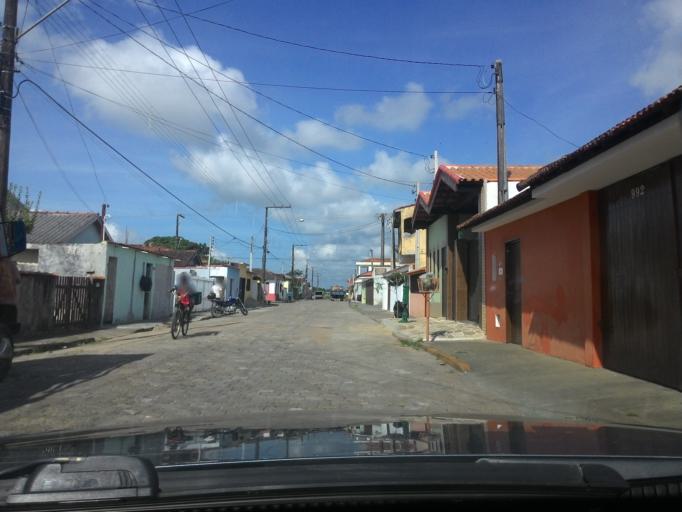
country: BR
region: Sao Paulo
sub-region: Iguape
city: Iguape
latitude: -24.7089
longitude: -47.5609
